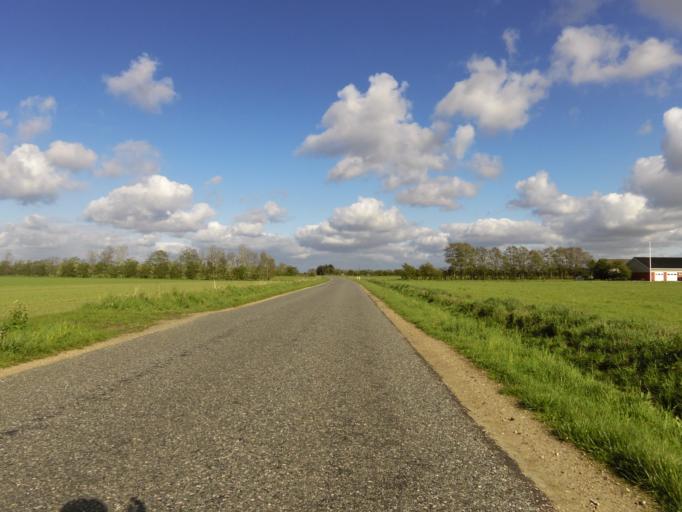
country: DK
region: South Denmark
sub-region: Esbjerg Kommune
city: Ribe
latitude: 55.2591
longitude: 8.7878
